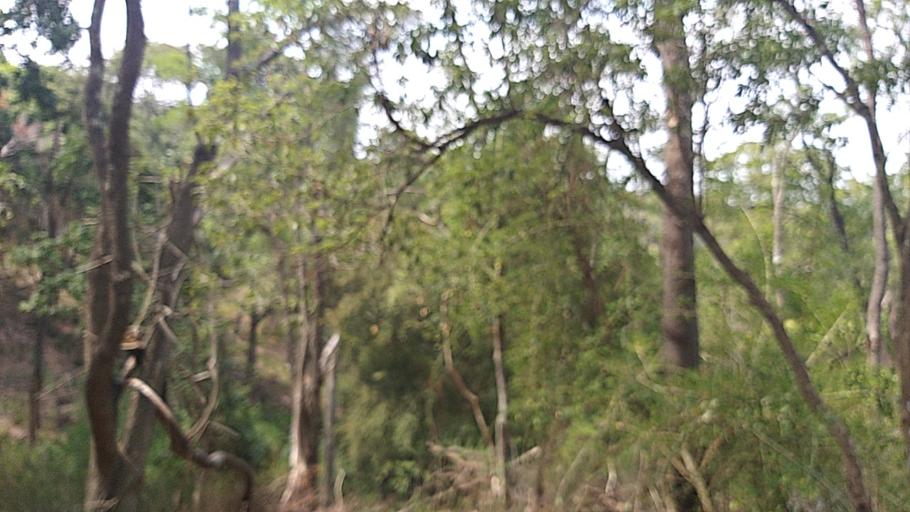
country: AU
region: New South Wales
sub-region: Wollongong
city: Mount Ousley
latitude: -34.4053
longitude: 150.8681
